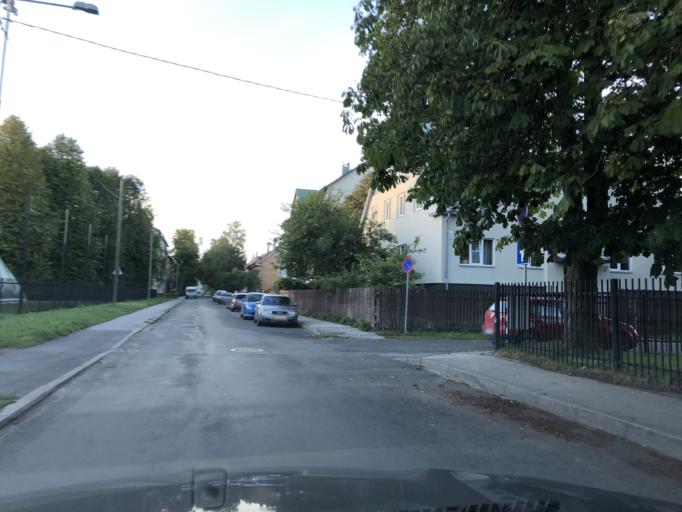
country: EE
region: Harju
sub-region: Tallinna linn
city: Tallinn
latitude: 59.4427
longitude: 24.7089
